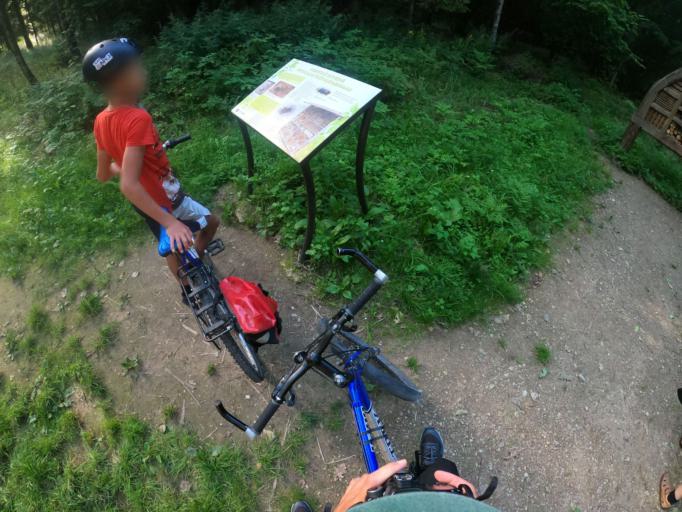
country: LT
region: Telsiu apskritis
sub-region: Telsiai
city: Telsiai
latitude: 55.9788
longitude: 22.1626
